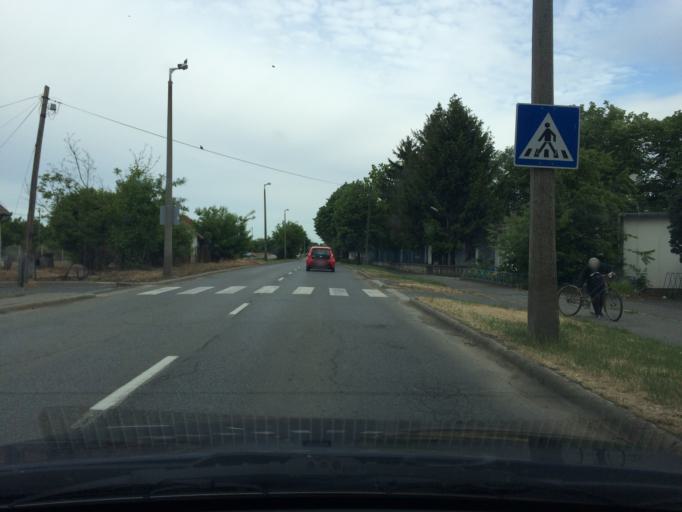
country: HU
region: Szabolcs-Szatmar-Bereg
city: Tiszavasvari
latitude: 47.9454
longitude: 21.3744
